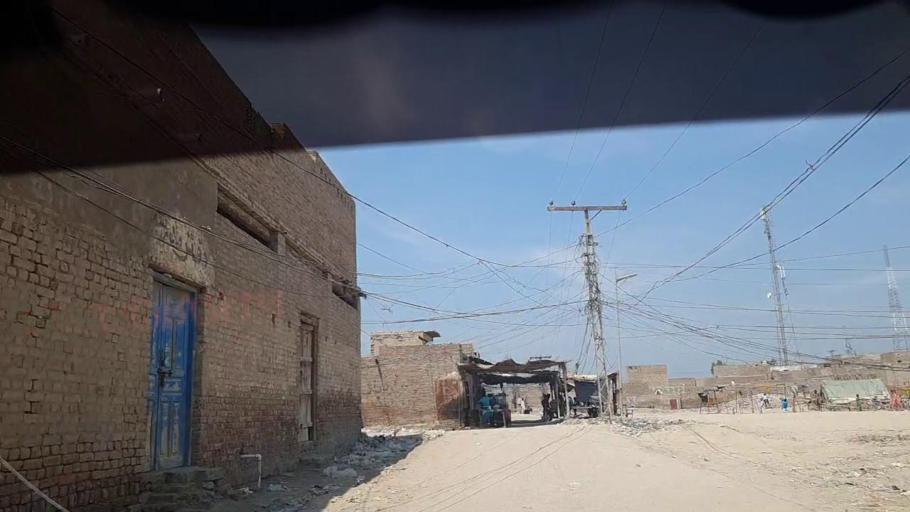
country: PK
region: Sindh
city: Thul
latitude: 28.1793
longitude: 68.7260
